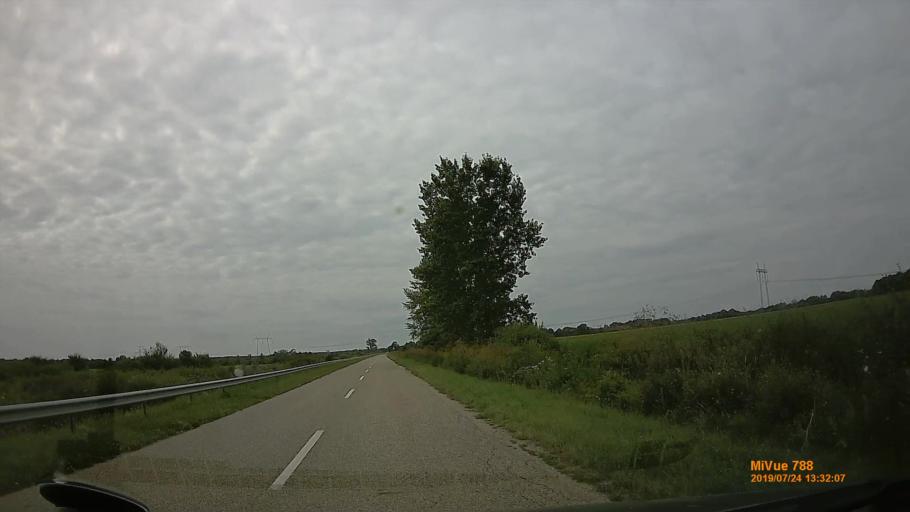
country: HU
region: Szabolcs-Szatmar-Bereg
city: Aranyosapati
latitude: 48.2296
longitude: 22.3456
